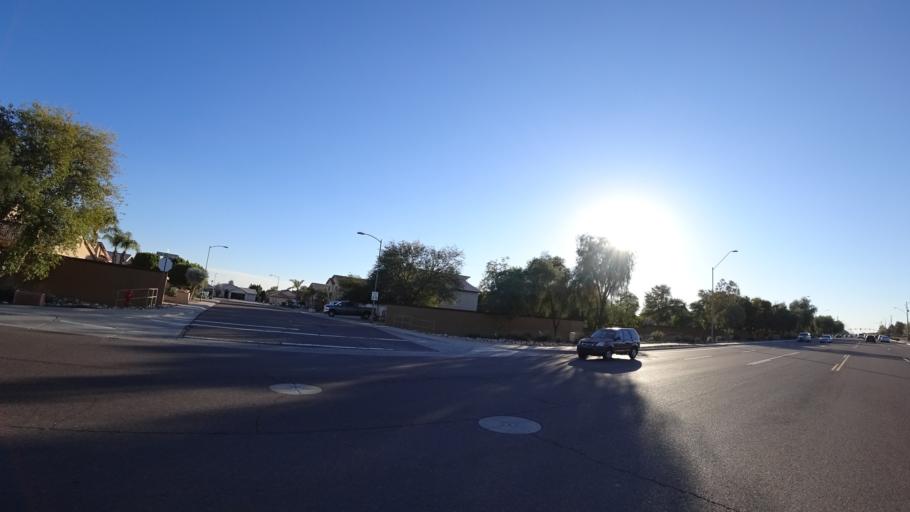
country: US
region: Arizona
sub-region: Maricopa County
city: Sun City
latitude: 33.6818
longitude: -112.2501
